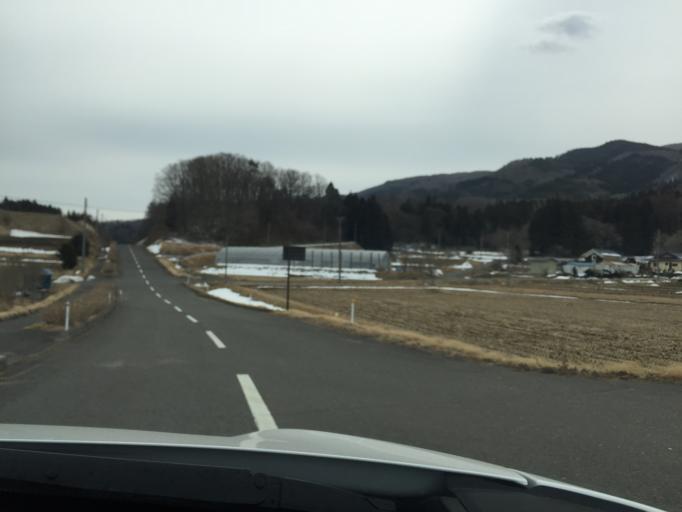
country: JP
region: Fukushima
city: Funehikimachi-funehiki
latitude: 37.3665
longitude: 140.5954
